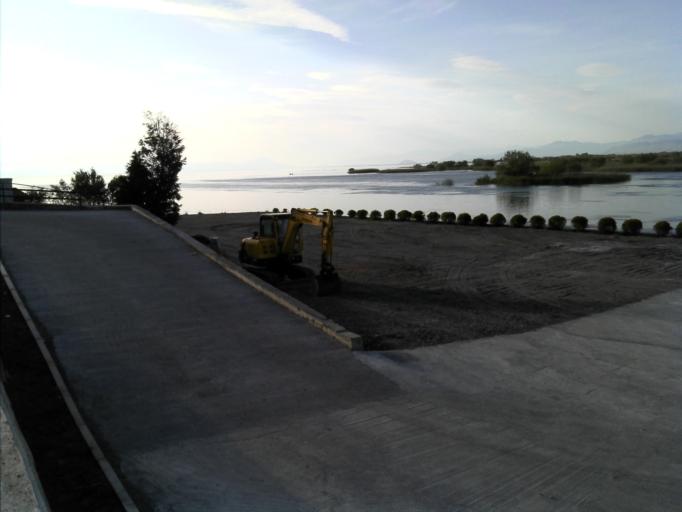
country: AL
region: Shkoder
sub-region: Rrethi i Shkodres
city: Shkoder
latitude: 42.0543
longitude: 19.4774
